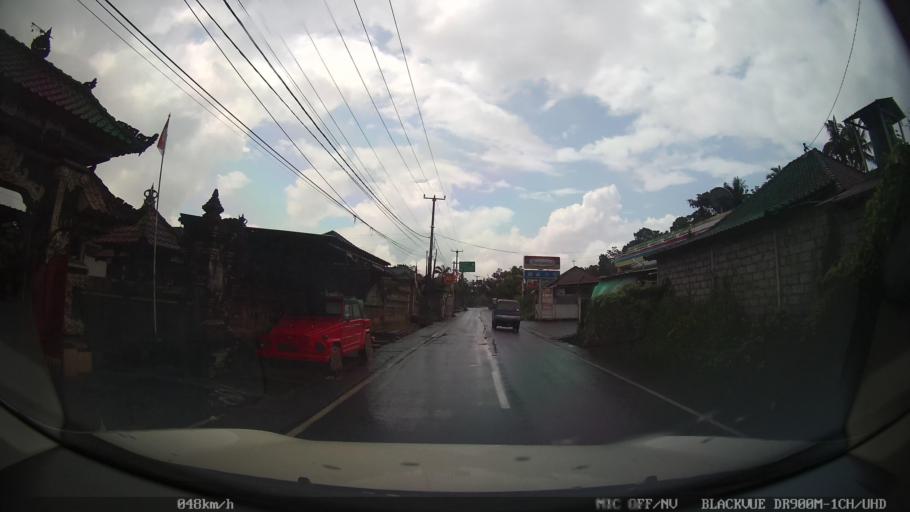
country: ID
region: Bali
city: Banjar Teguan
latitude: -8.5068
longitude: 115.2303
